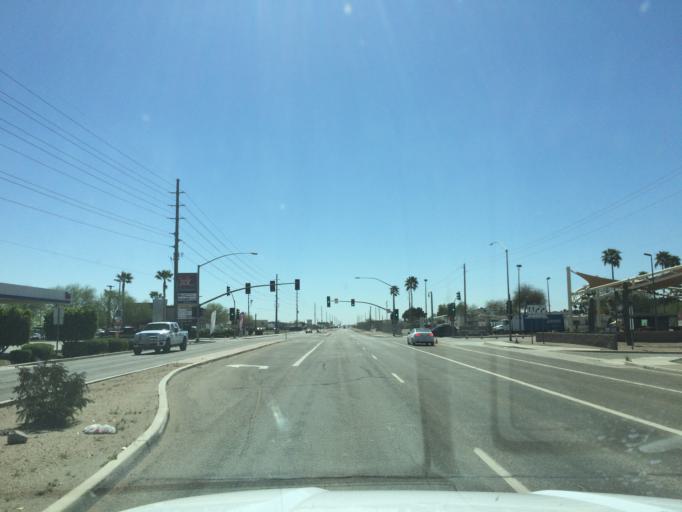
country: US
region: Arizona
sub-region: Yuma County
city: Yuma
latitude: 32.6572
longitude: -114.5812
